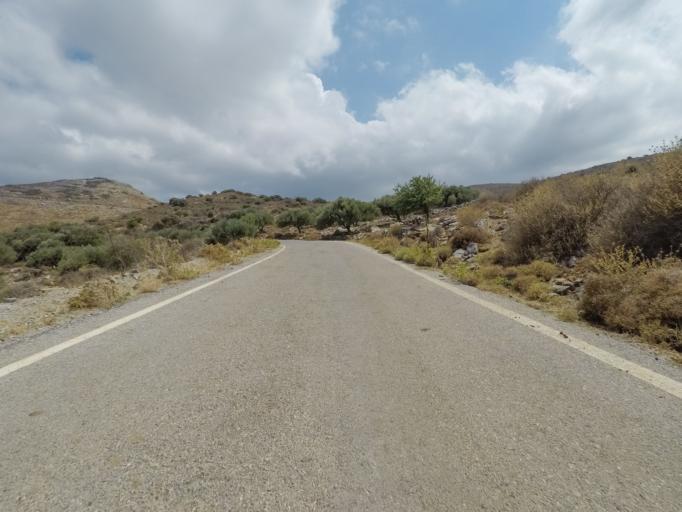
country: GR
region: Crete
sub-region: Nomos Lasithiou
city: Elounda
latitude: 35.3157
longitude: 25.6758
